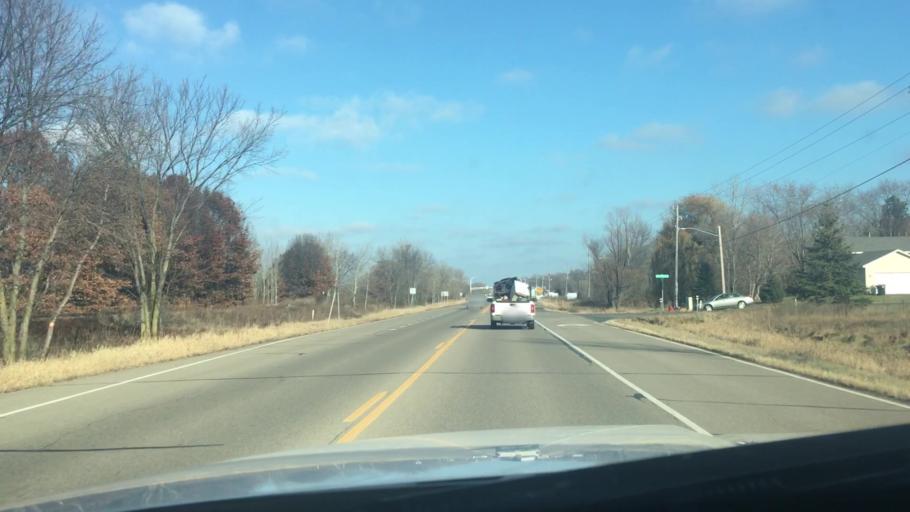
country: US
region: Minnesota
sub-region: Washington County
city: Hugo
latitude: 45.1480
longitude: -92.9967
